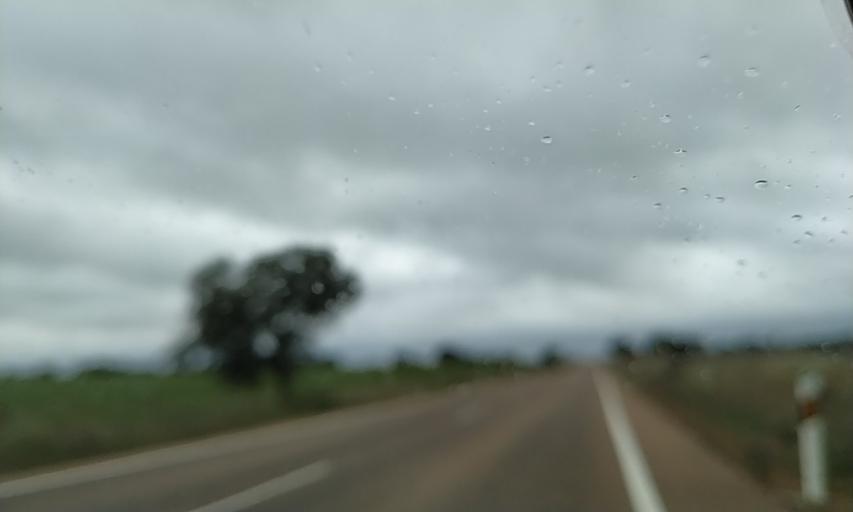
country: ES
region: Extremadura
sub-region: Provincia de Badajoz
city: Villar del Rey
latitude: 39.0194
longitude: -6.8481
